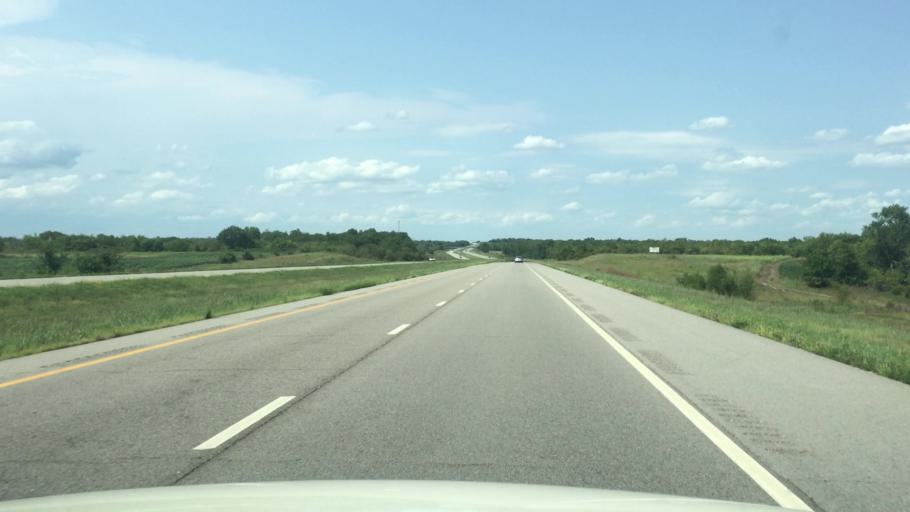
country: US
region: Kansas
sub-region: Linn County
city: La Cygne
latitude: 38.4442
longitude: -94.6862
